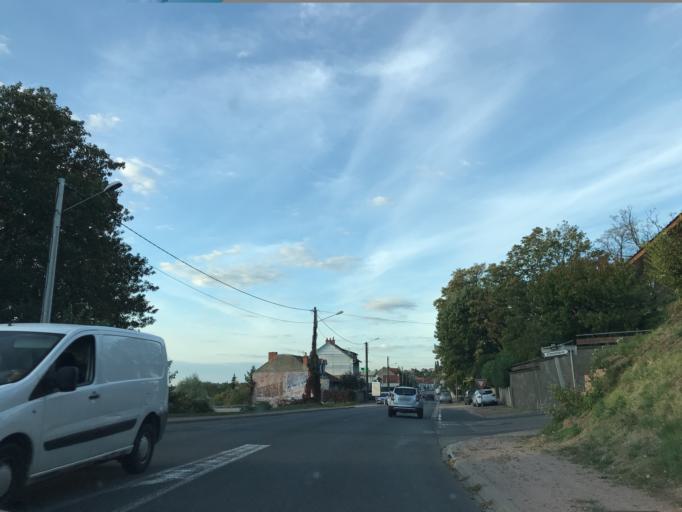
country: FR
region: Auvergne
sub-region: Departement de l'Allier
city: Abrest
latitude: 46.1005
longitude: 3.4437
